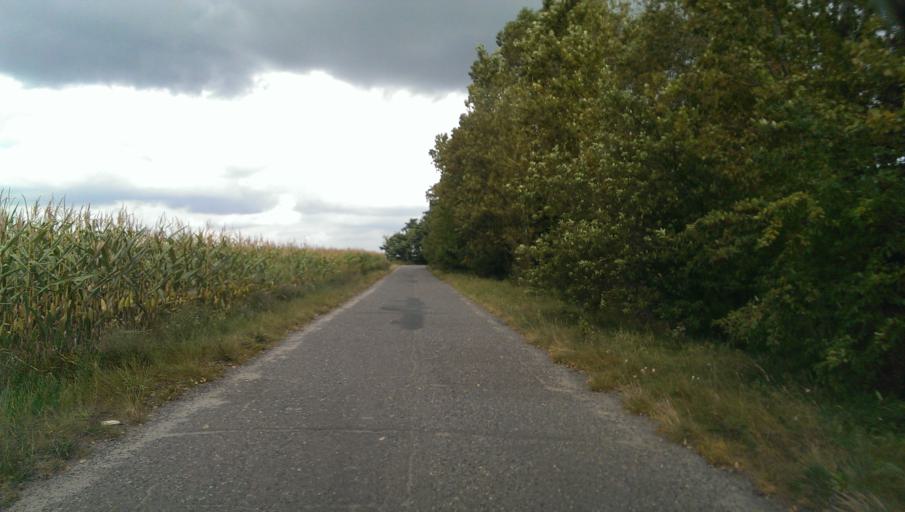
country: DE
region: Brandenburg
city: Rangsdorf
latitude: 52.2966
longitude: 13.4763
